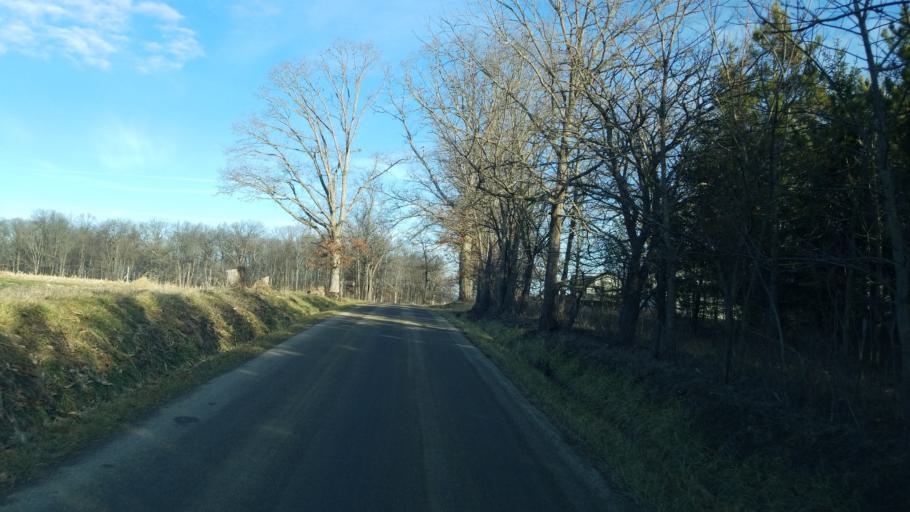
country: US
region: Ohio
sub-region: Knox County
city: Gambier
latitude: 40.3593
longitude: -82.4330
